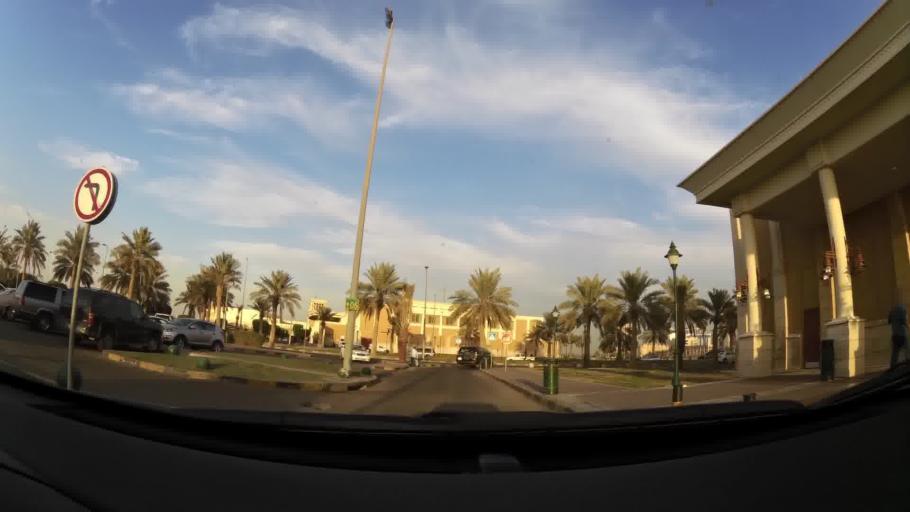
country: KW
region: Al Asimah
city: Kuwait City
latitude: 29.3875
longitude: 47.9792
